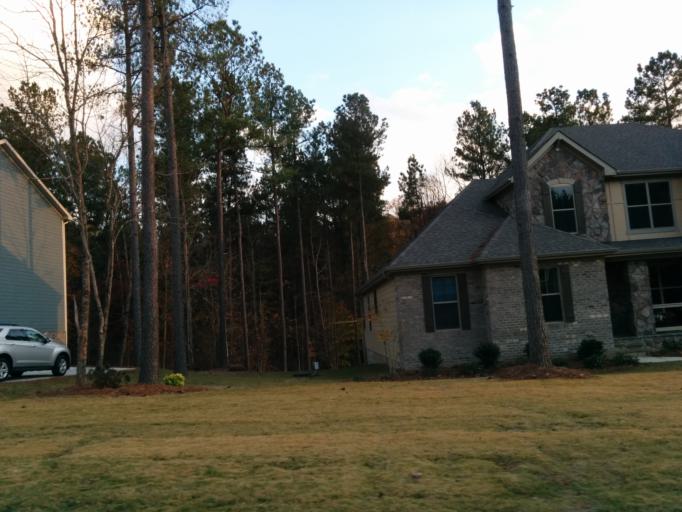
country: US
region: North Carolina
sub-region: Iredell County
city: Troutman
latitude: 35.6423
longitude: -80.8902
